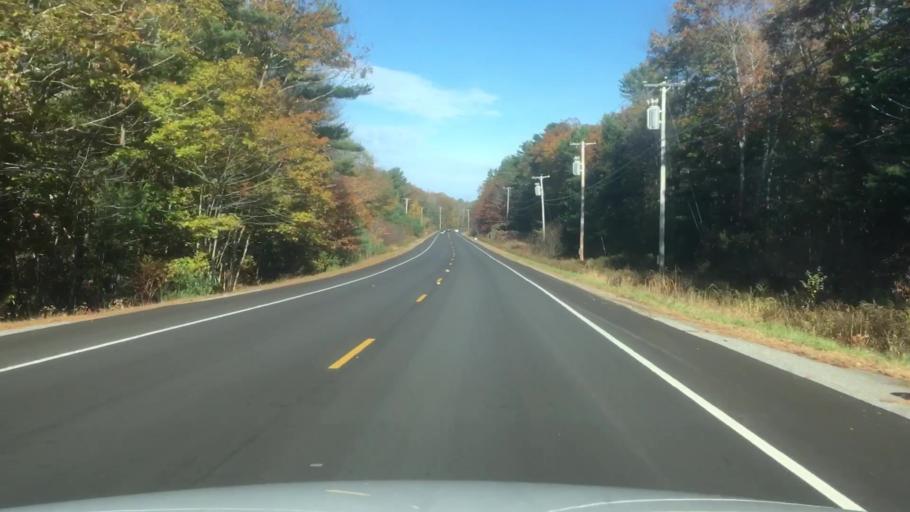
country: US
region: Maine
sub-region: Sagadahoc County
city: Woolwich
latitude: 43.8785
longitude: -69.7868
